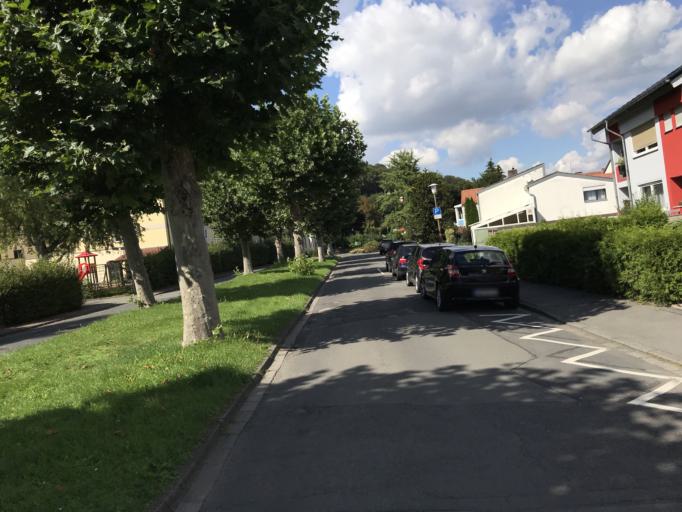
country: DE
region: Hesse
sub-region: Regierungsbezirk Kassel
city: Bad Sooden-Allendorf
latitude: 51.2652
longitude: 9.9657
